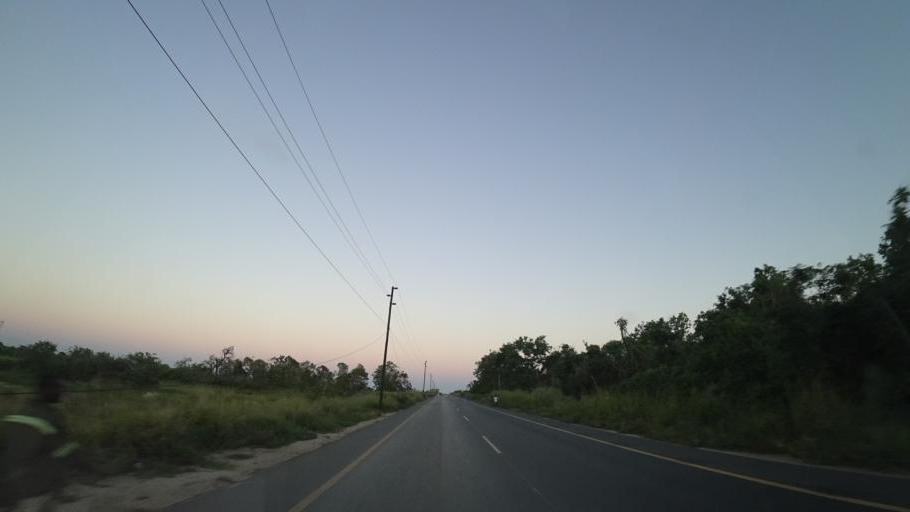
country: MZ
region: Sofala
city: Dondo
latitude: -19.5029
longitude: 34.6011
